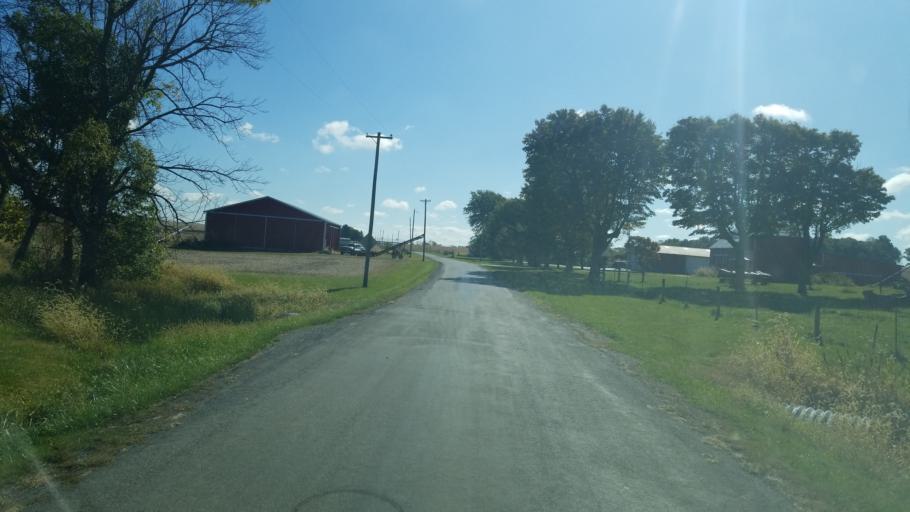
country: US
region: Ohio
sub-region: Highland County
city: Leesburg
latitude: 39.2803
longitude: -83.5726
